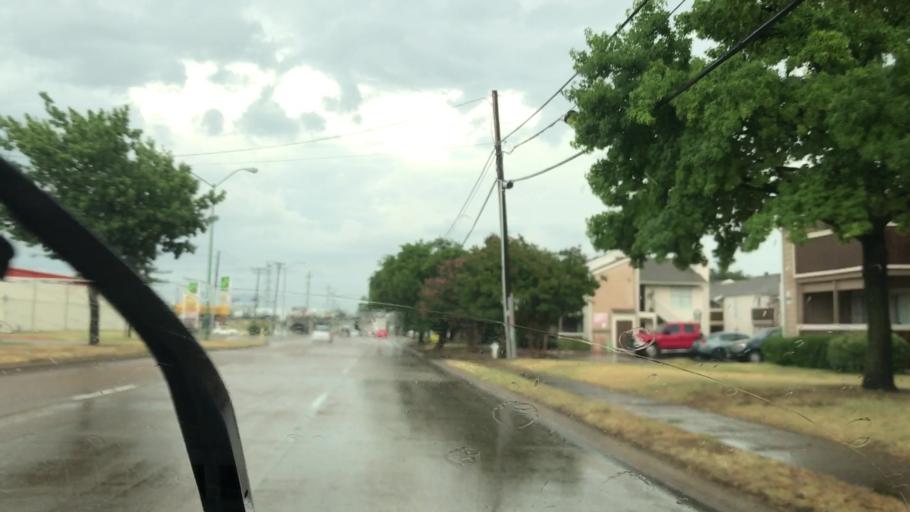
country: US
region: Texas
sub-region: Dallas County
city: Garland
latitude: 32.8787
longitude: -96.6923
